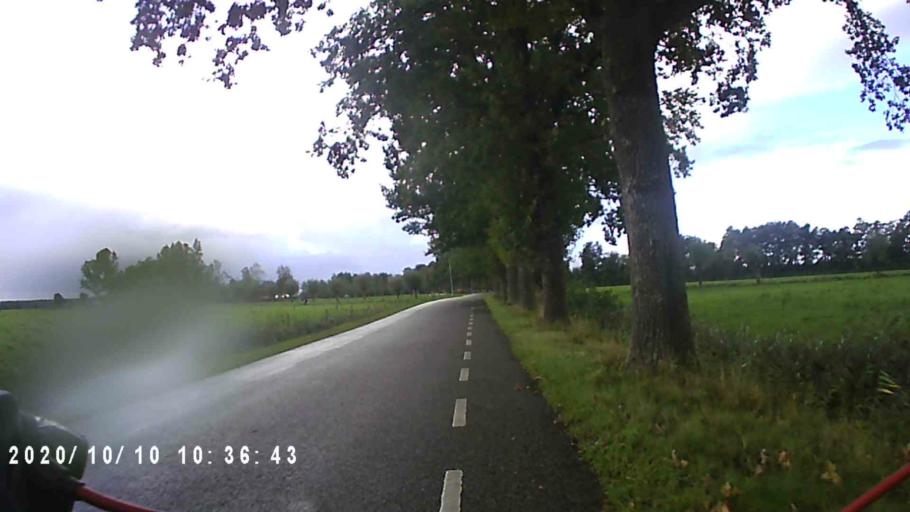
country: NL
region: Groningen
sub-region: Gemeente Grootegast
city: Grootegast
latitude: 53.1861
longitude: 6.3027
